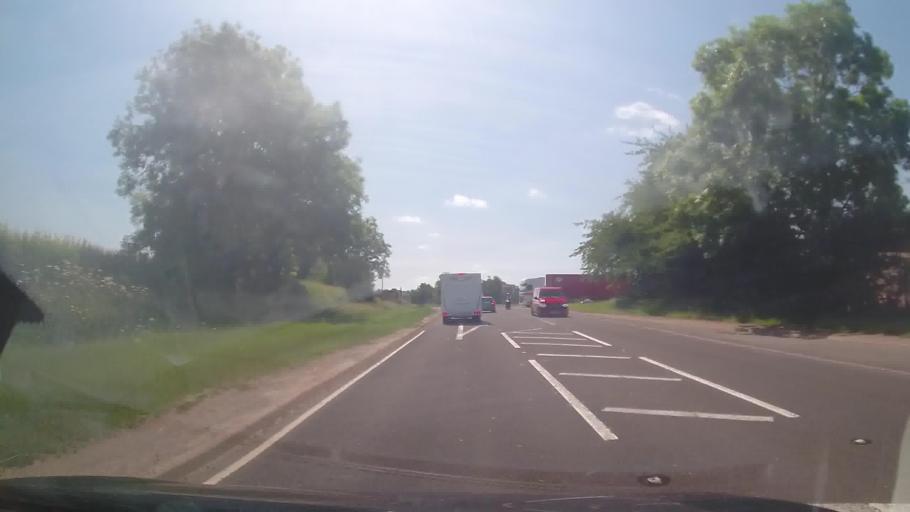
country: GB
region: England
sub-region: Herefordshire
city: Orleton
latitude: 52.3133
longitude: -2.7058
